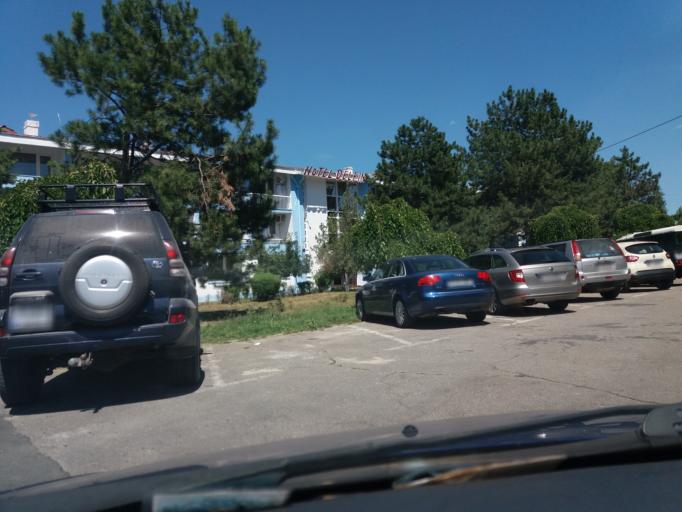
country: RO
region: Constanta
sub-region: Comuna Navodari
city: Navodari
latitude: 44.3199
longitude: 28.6287
